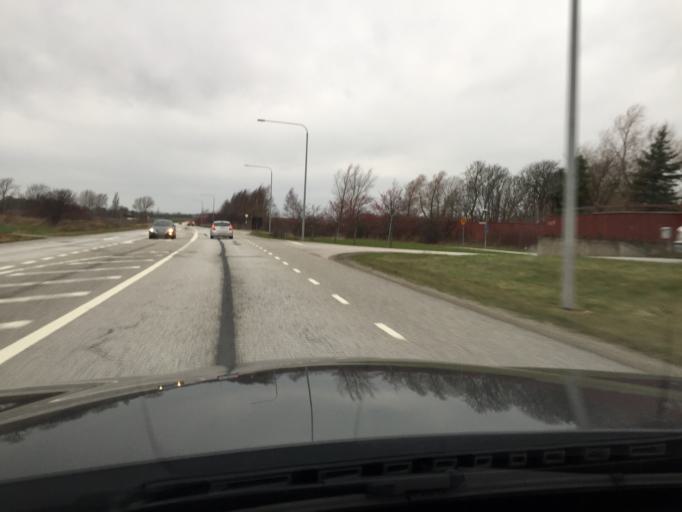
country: SE
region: Skane
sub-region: Malmo
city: Oxie
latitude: 55.5835
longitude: 13.1348
